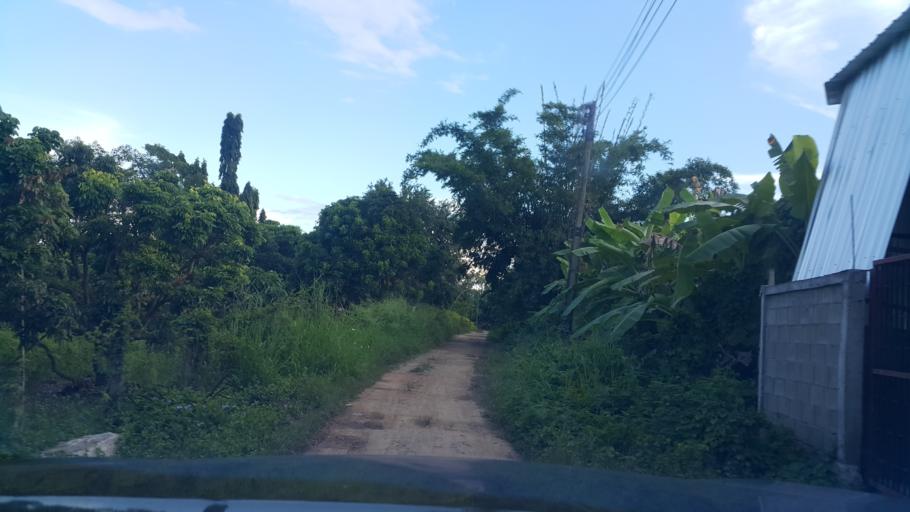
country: TH
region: Chiang Mai
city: Mae Taeng
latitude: 19.1629
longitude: 99.0081
